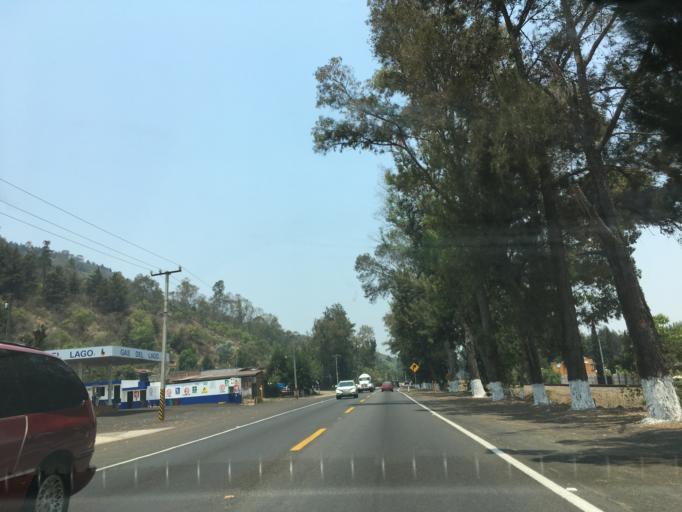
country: MX
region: Michoacan
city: Patzcuaro
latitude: 19.5462
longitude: -101.5974
